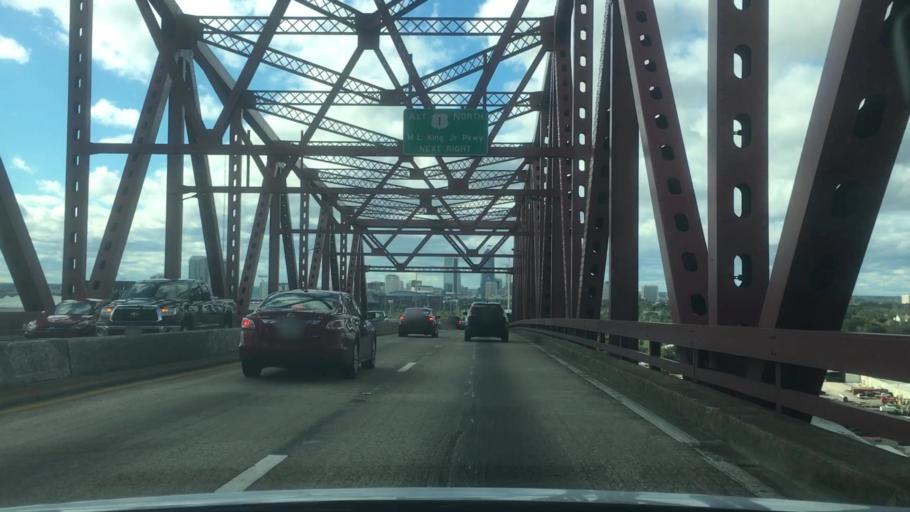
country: US
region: Florida
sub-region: Duval County
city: Jacksonville
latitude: 30.3273
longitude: -81.6257
